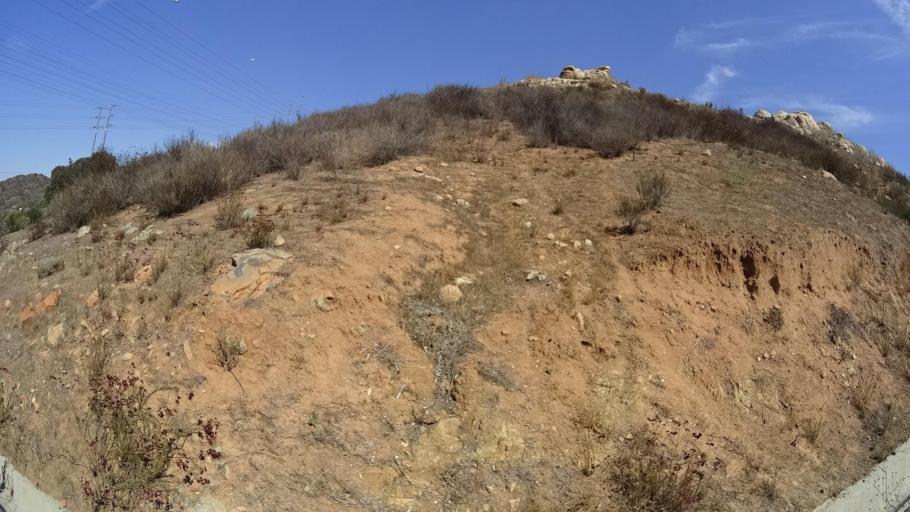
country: US
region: California
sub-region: San Diego County
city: Rancho San Diego
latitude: 32.7213
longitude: -116.9302
